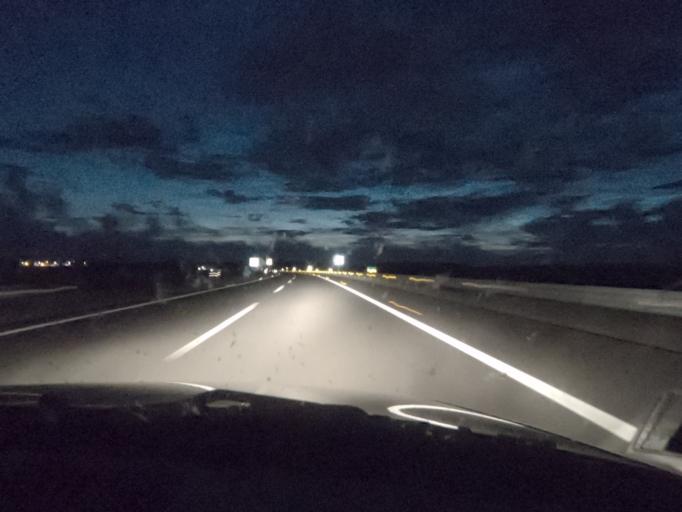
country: ES
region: Extremadura
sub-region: Provincia de Caceres
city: Morcillo
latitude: 39.9896
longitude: -6.4398
